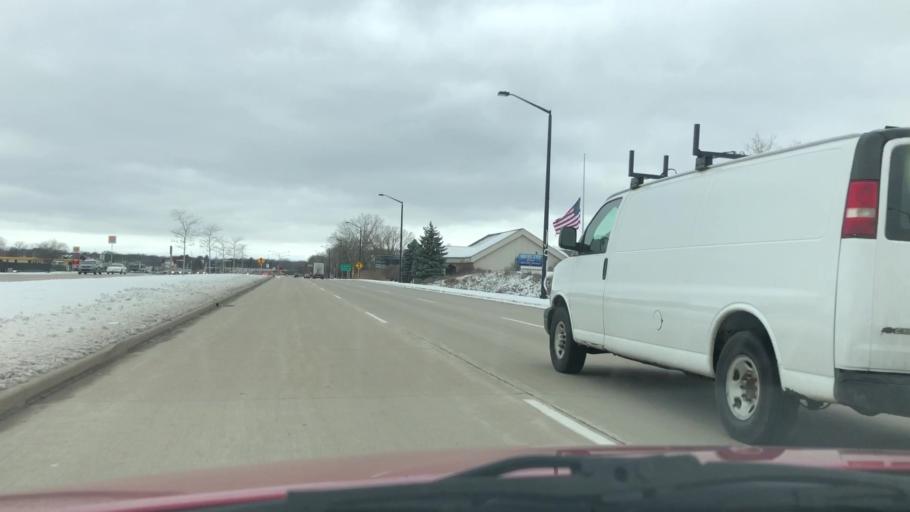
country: US
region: Wisconsin
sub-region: Brown County
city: Ashwaubenon
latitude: 44.5052
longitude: -88.0671
